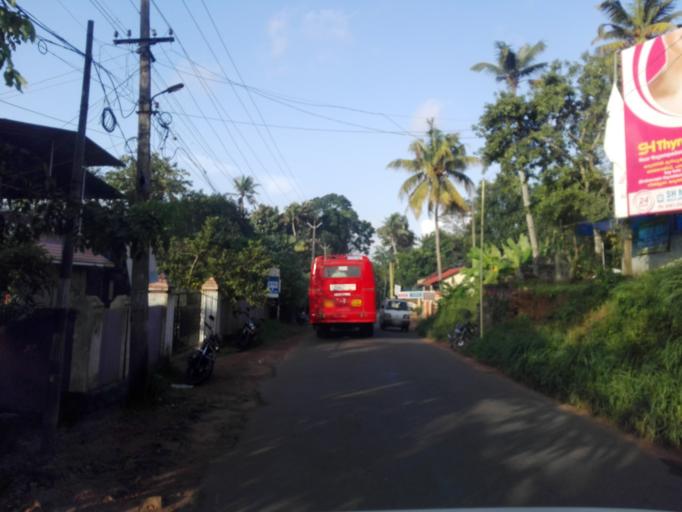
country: IN
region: Kerala
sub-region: Kottayam
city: Kottayam
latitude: 9.6120
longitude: 76.5029
